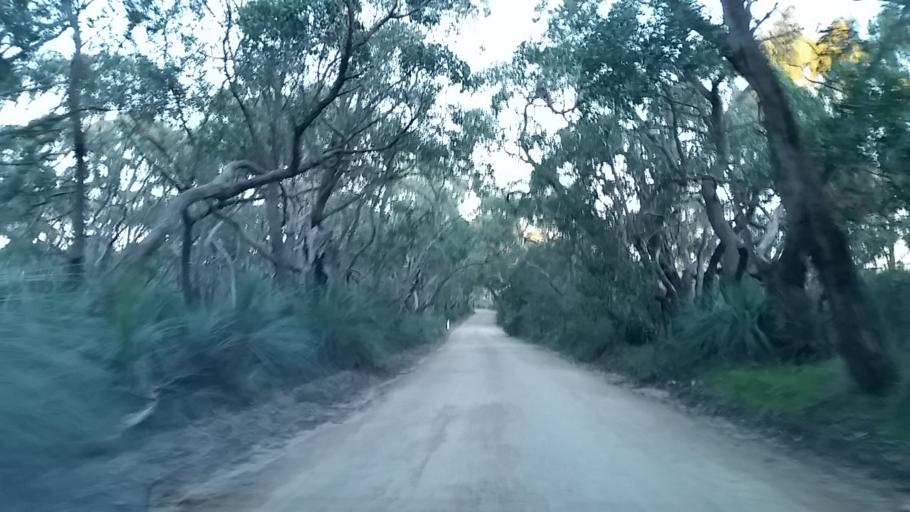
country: AU
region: South Australia
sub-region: Alexandrina
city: Mount Compass
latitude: -35.2786
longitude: 138.5932
